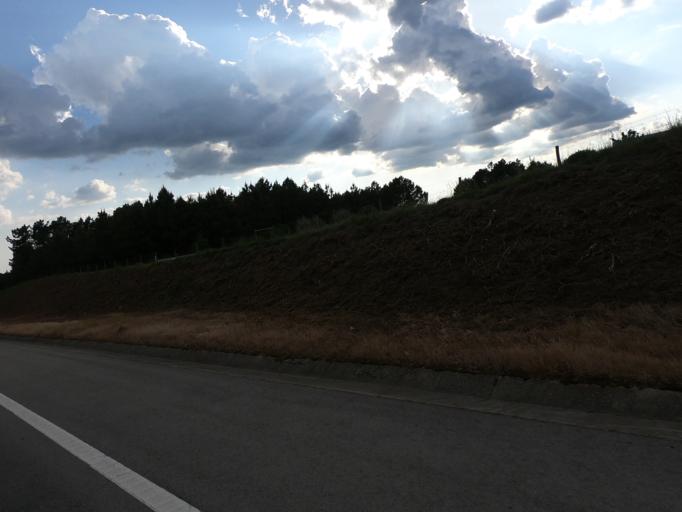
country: PT
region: Vila Real
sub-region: Vila Real
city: Vila Real
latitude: 41.2668
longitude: -7.7007
